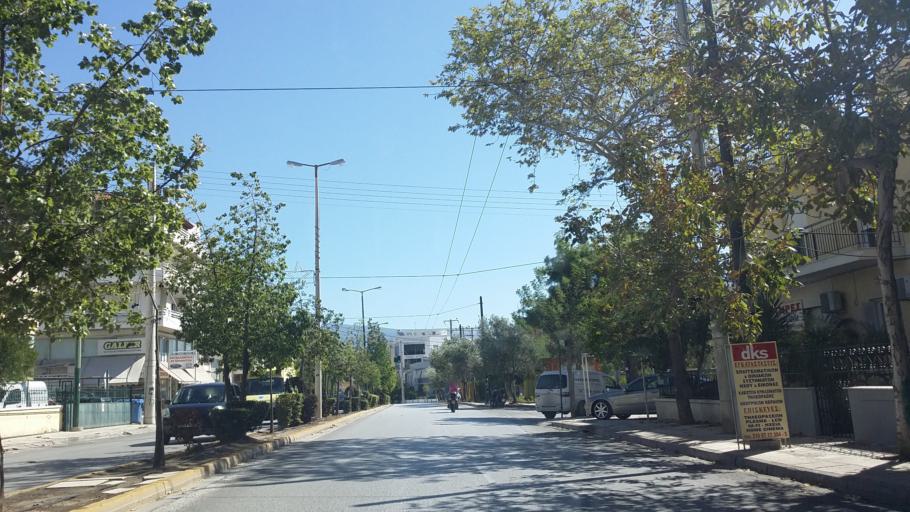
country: GR
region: Attica
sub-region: Nomarchia Athinas
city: Peristeri
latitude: 38.0163
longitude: 23.7015
